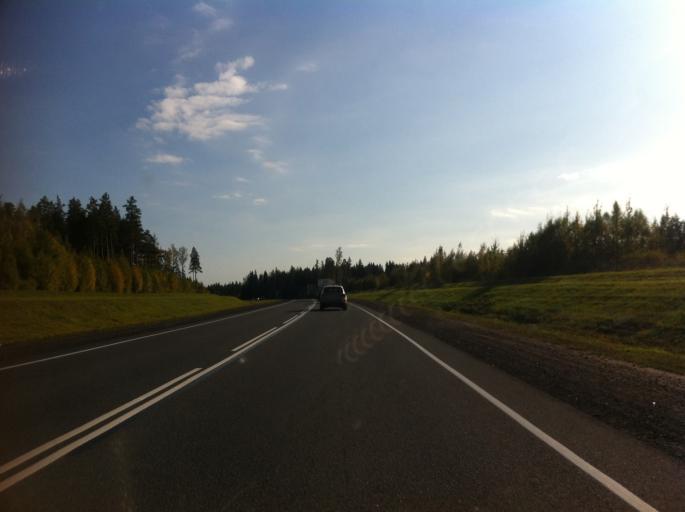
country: RU
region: Leningrad
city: Luga
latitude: 58.7660
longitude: 29.8819
